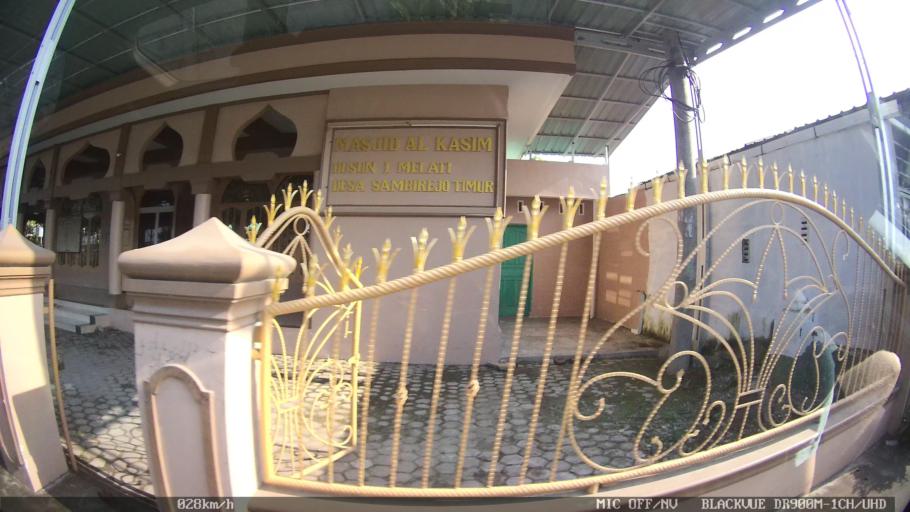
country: ID
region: North Sumatra
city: Medan
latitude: 3.5937
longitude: 98.7569
